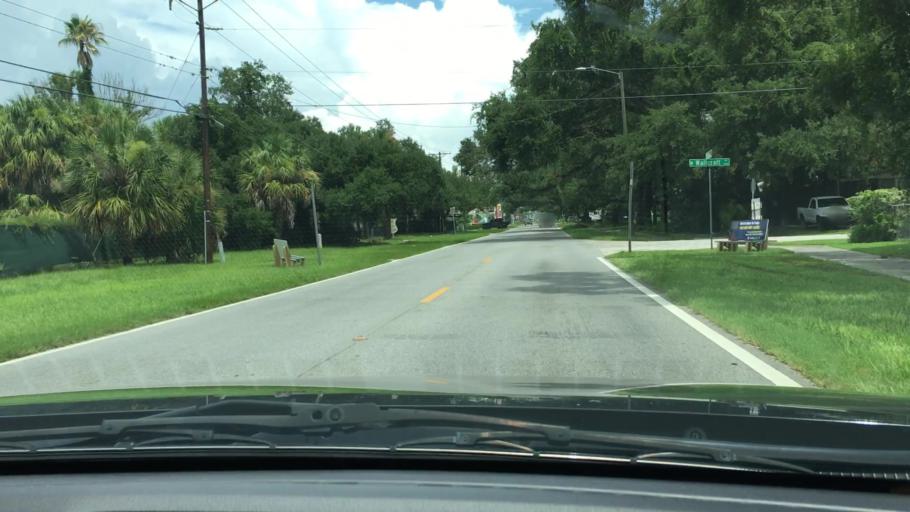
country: US
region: Florida
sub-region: Hillsborough County
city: Tampa
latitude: 27.9027
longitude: -82.5267
